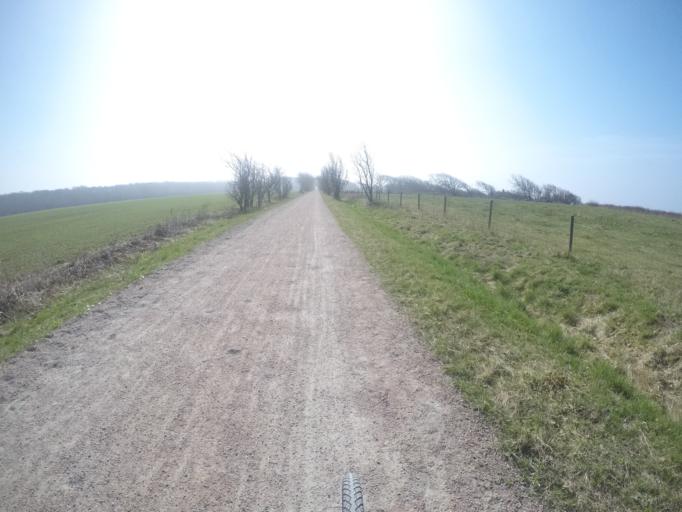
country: SE
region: Skane
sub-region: Hoganas Kommun
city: Hoganas
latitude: 56.2635
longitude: 12.5174
